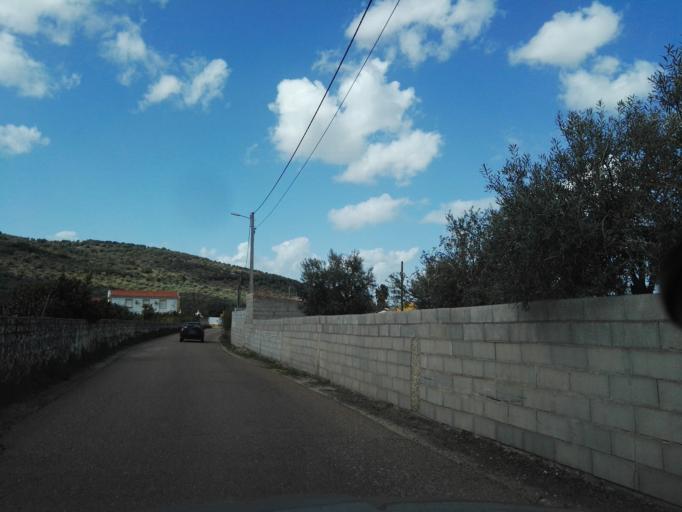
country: PT
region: Portalegre
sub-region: Elvas
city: Elvas
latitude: 38.8900
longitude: -7.1560
